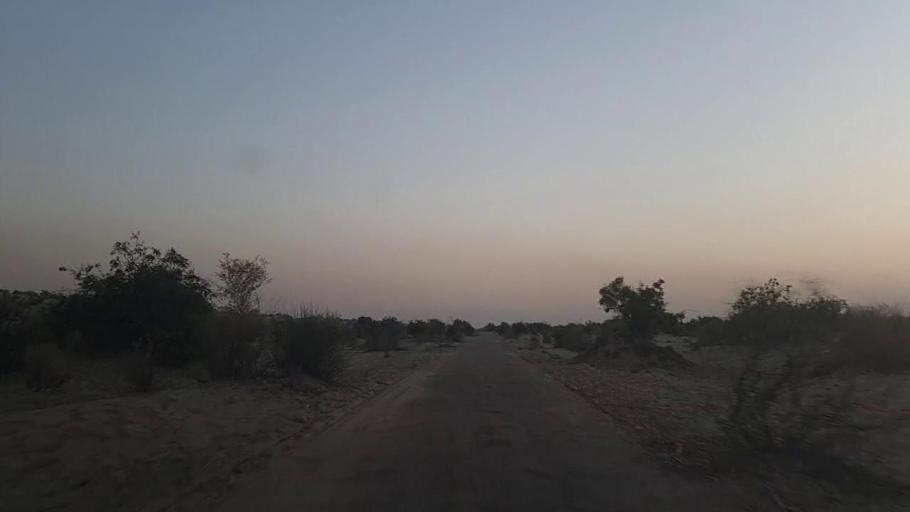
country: PK
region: Sindh
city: Jam Sahib
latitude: 26.3989
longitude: 68.8096
